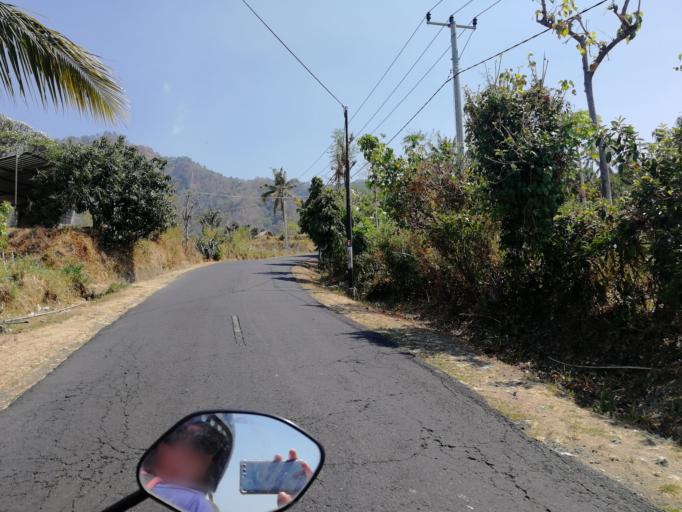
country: ID
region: Bali
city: Banjar Trunyan
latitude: -8.1352
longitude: 115.3235
